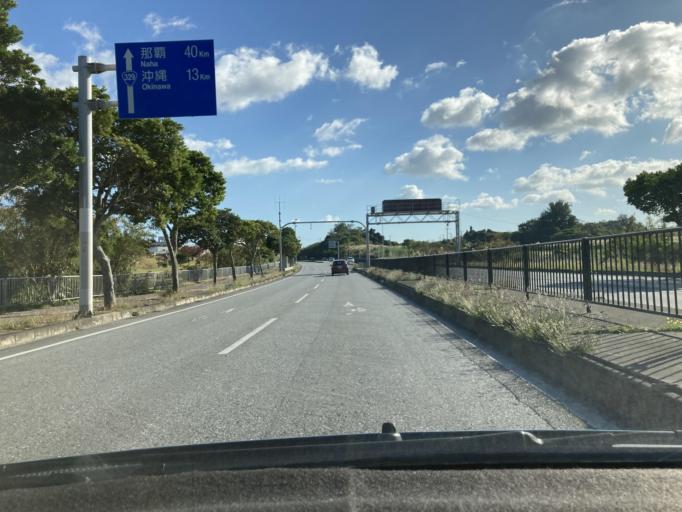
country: JP
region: Okinawa
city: Ishikawa
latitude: 26.4193
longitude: 127.8155
